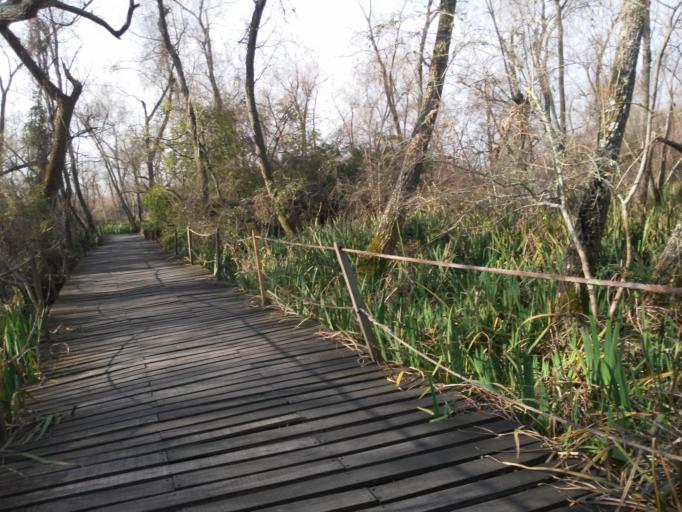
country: AR
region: Buenos Aires
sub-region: Partido de Avellaneda
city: Avellaneda
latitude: -34.6629
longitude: -58.3137
